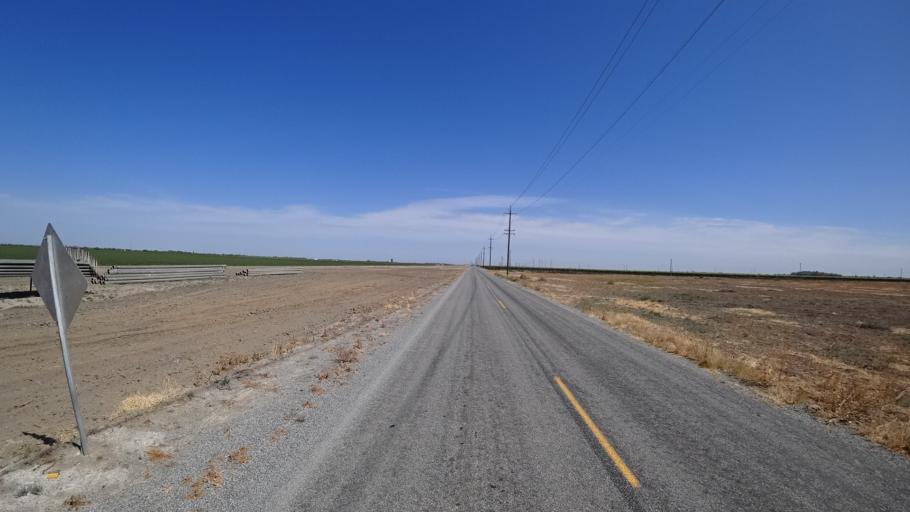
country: US
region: California
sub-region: Kings County
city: Stratford
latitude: 36.2319
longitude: -119.8343
